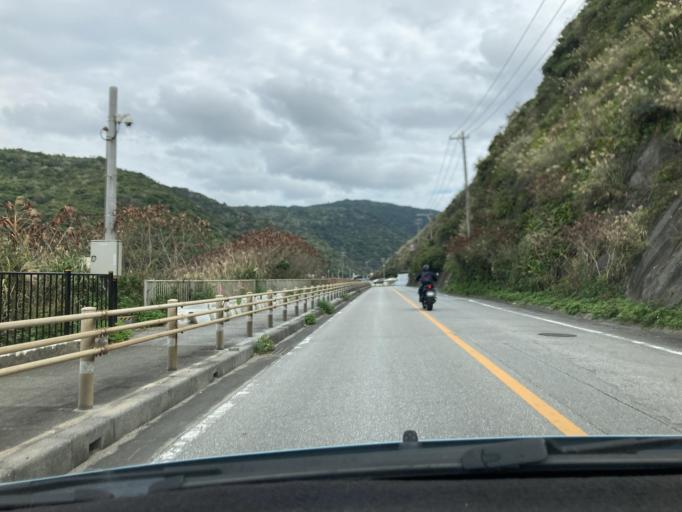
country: JP
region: Okinawa
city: Nago
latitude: 26.7973
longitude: 128.2295
